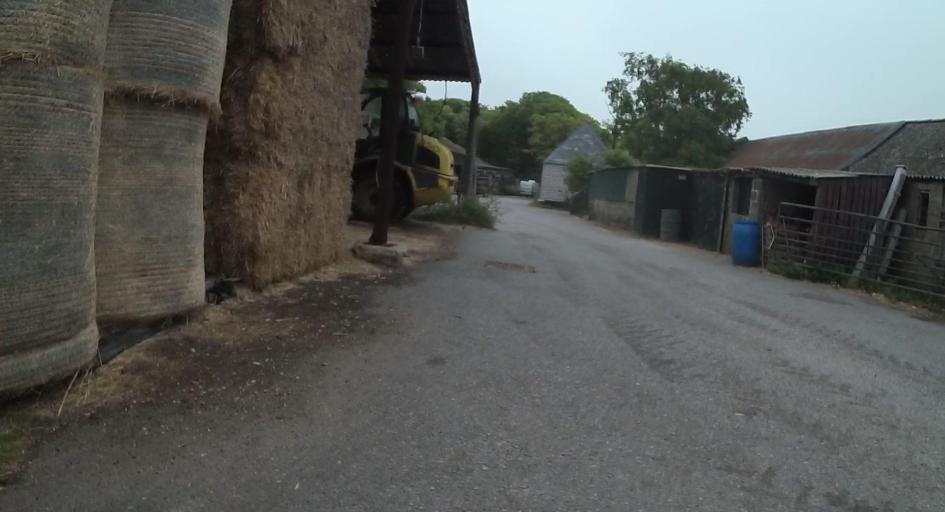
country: GB
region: England
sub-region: Dorset
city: Wareham
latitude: 50.6457
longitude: -2.0727
